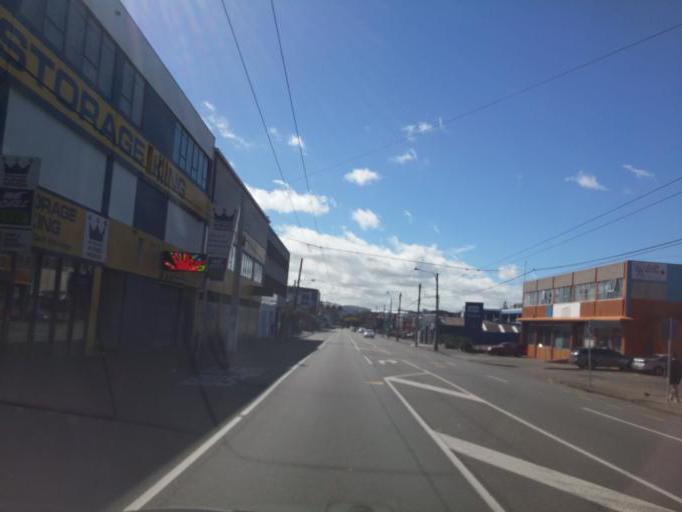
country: NZ
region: Wellington
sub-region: Wellington City
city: Wellington
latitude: -41.3047
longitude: 174.7787
